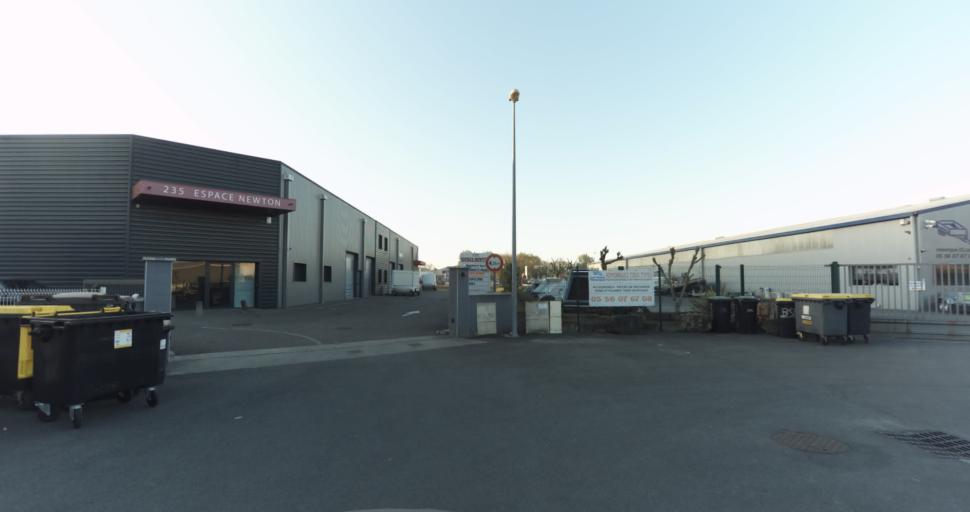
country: FR
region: Aquitaine
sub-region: Departement de la Gironde
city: Martignas-sur-Jalle
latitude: 44.8133
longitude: -0.7465
